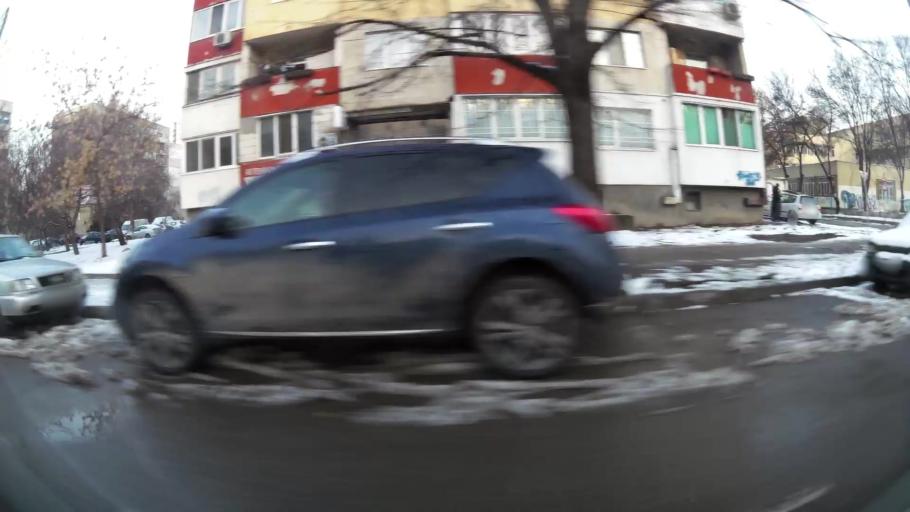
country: BG
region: Sofia-Capital
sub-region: Stolichna Obshtina
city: Sofia
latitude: 42.6866
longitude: 23.3716
